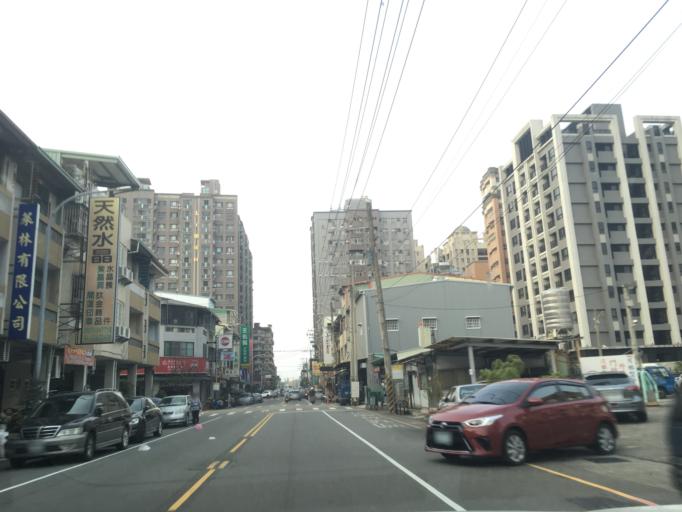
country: TW
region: Taiwan
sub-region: Taichung City
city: Taichung
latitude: 24.1820
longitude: 120.6951
